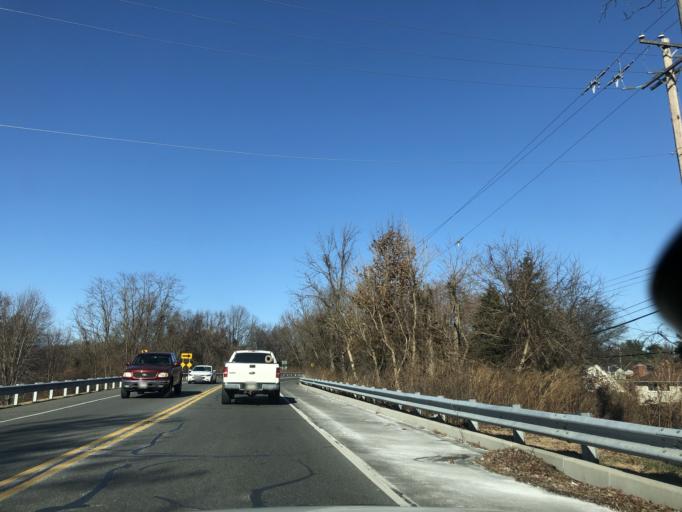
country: US
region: Pennsylvania
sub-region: Bucks County
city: Langhorne Manor
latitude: 40.1638
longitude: -74.8978
